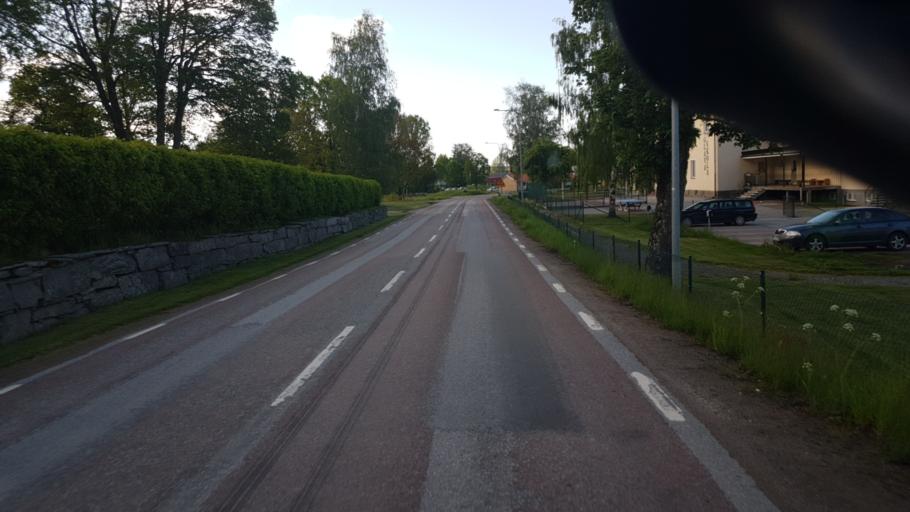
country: SE
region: Vaermland
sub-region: Arvika Kommun
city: Arvika
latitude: 59.5562
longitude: 12.5611
